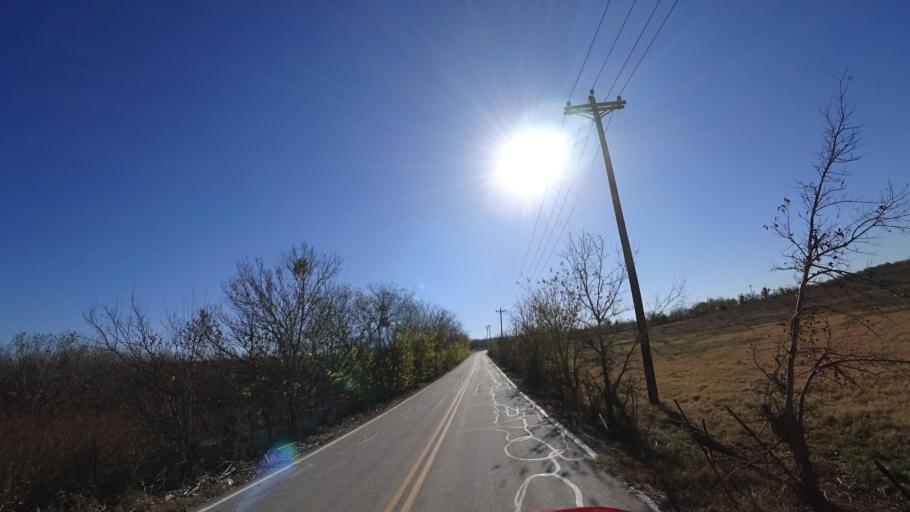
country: US
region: Texas
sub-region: Travis County
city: Onion Creek
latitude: 30.1124
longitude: -97.6712
